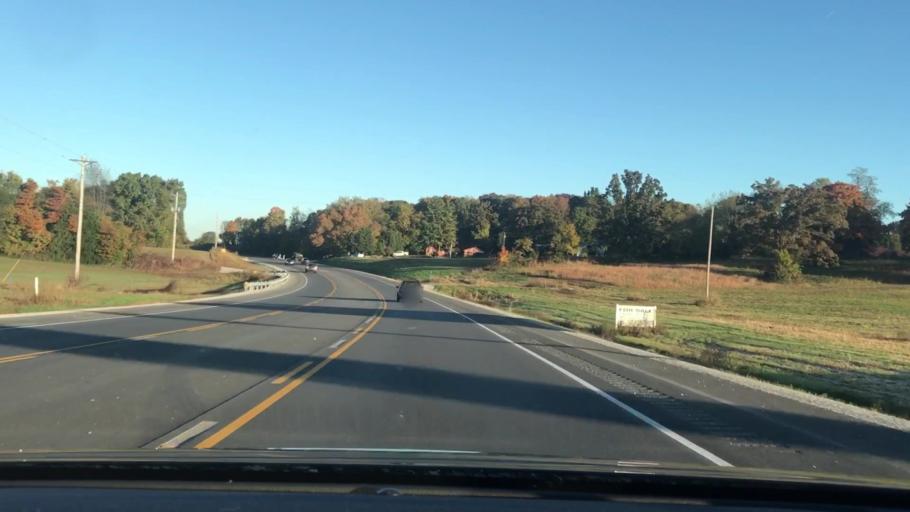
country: US
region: Kentucky
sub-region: Simpson County
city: Franklin
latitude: 36.6720
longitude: -86.5589
